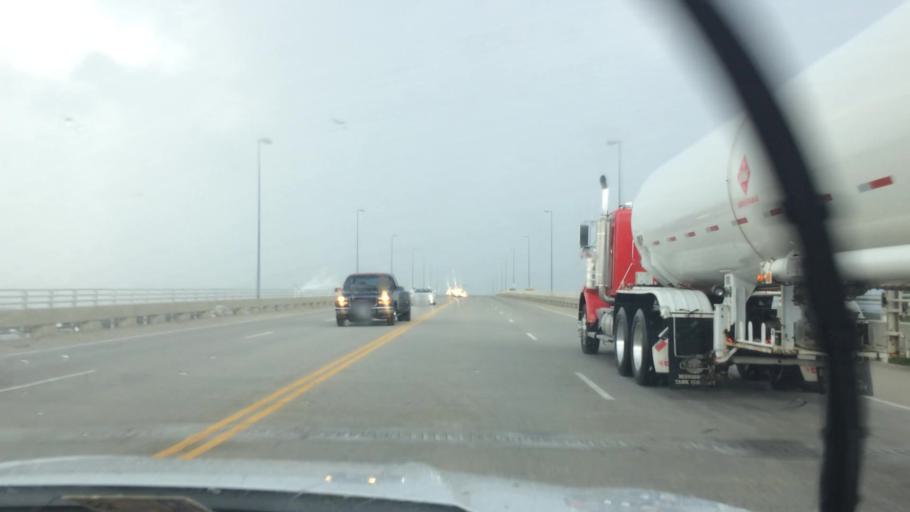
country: US
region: Virginia
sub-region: King William County
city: West Point
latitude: 37.5354
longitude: -76.7833
